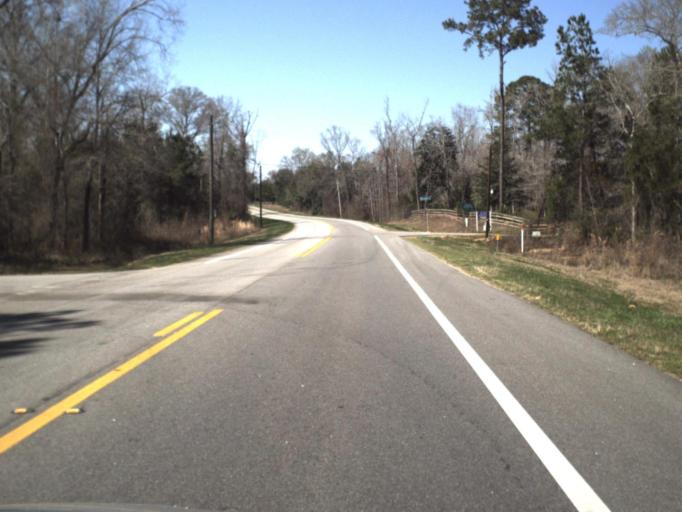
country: US
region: Florida
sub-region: Jackson County
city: Marianna
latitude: 30.8025
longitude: -85.2789
